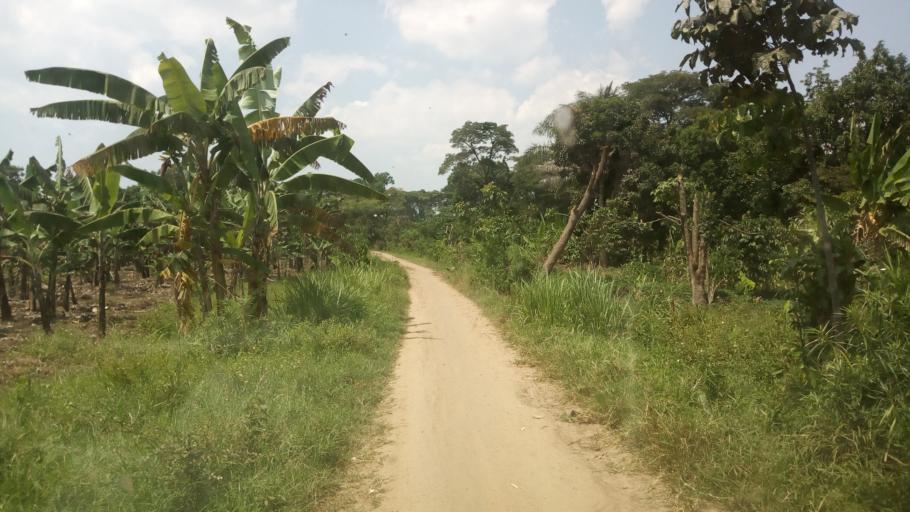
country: UG
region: Western Region
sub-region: Kanungu District
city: Ntungamo
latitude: -0.7784
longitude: 29.6491
